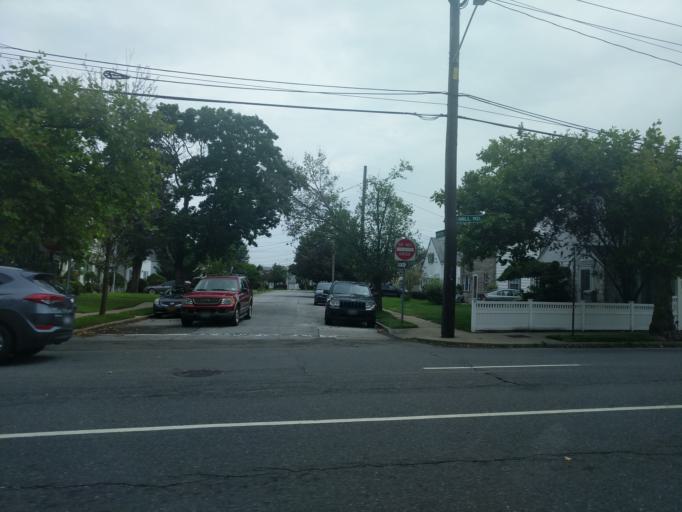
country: US
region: New York
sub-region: Nassau County
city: South Valley Stream
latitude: 40.6497
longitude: -73.7084
